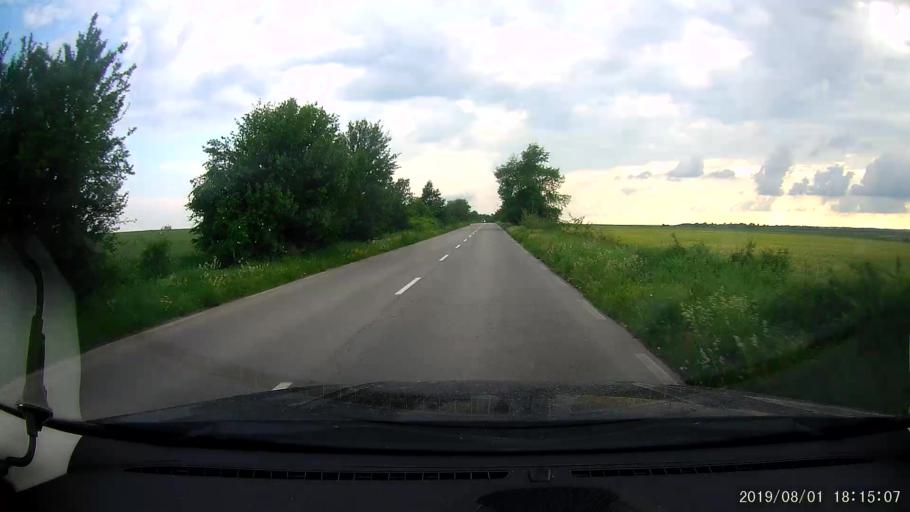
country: BG
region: Silistra
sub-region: Obshtina Dulovo
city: Dulovo
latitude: 43.7586
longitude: 27.1116
